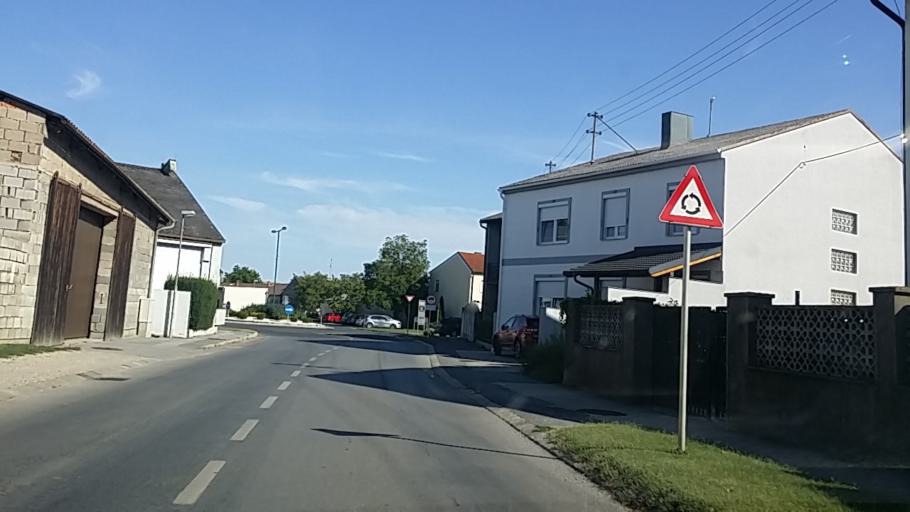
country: AT
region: Burgenland
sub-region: Politischer Bezirk Neusiedl am See
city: Pamhagen
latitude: 47.6994
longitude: 16.9097
